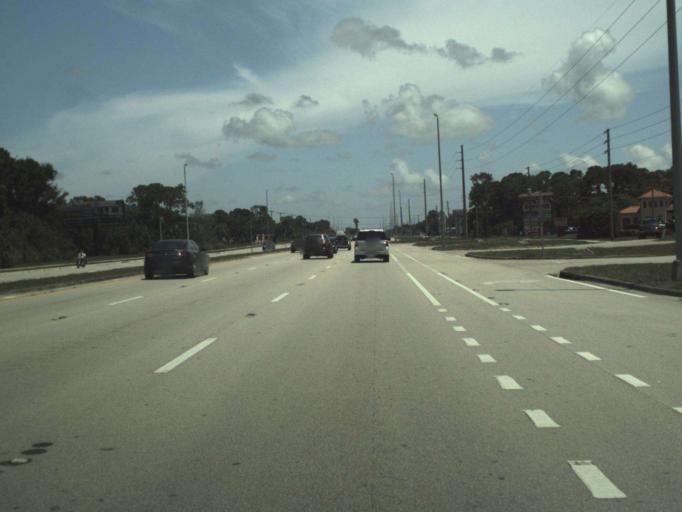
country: US
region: Florida
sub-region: Saint Lucie County
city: River Park
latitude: 27.3191
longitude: -80.3165
